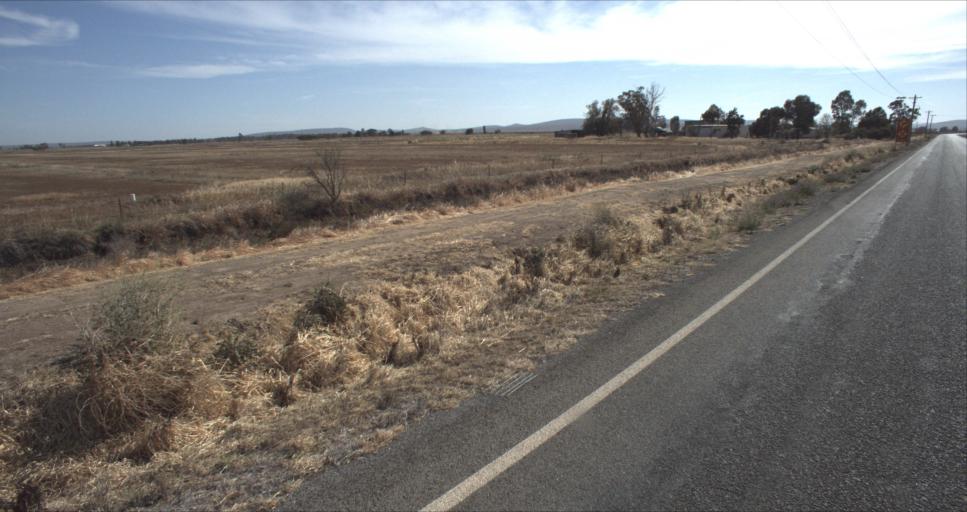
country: AU
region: New South Wales
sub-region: Leeton
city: Leeton
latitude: -34.5577
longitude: 146.4458
